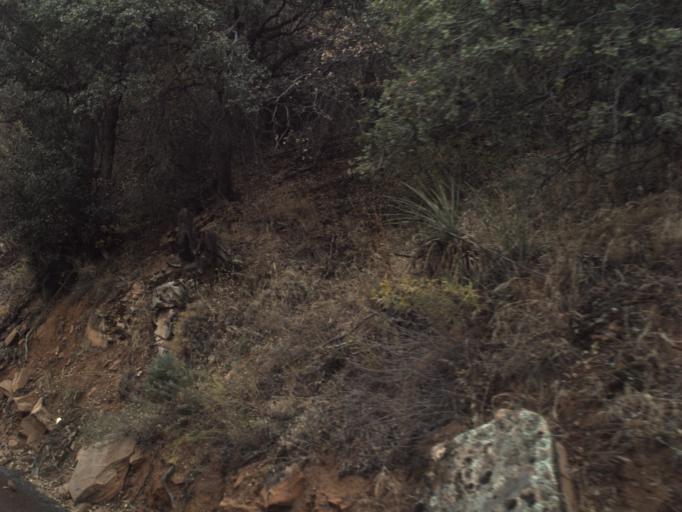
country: US
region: Utah
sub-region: Washington County
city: Hildale
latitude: 37.2156
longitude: -112.9611
